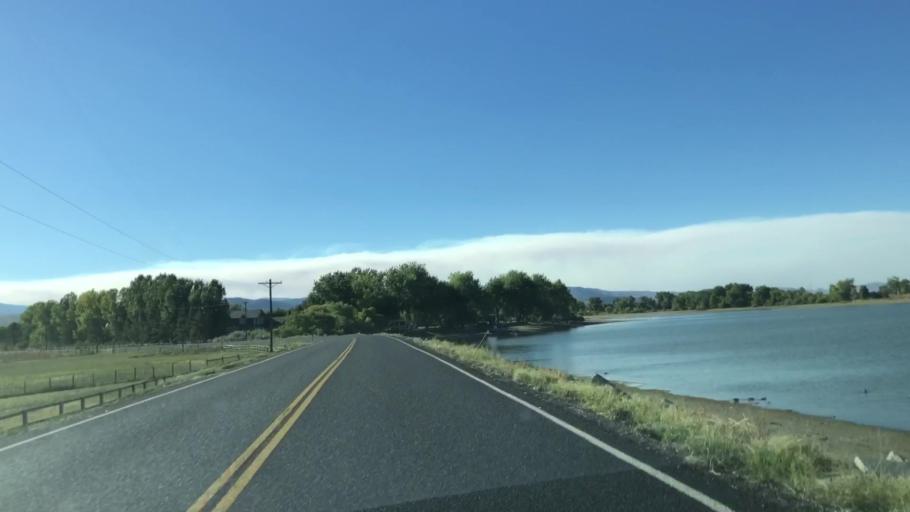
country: US
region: Colorado
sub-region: Larimer County
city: Loveland
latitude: 40.4614
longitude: -105.0542
